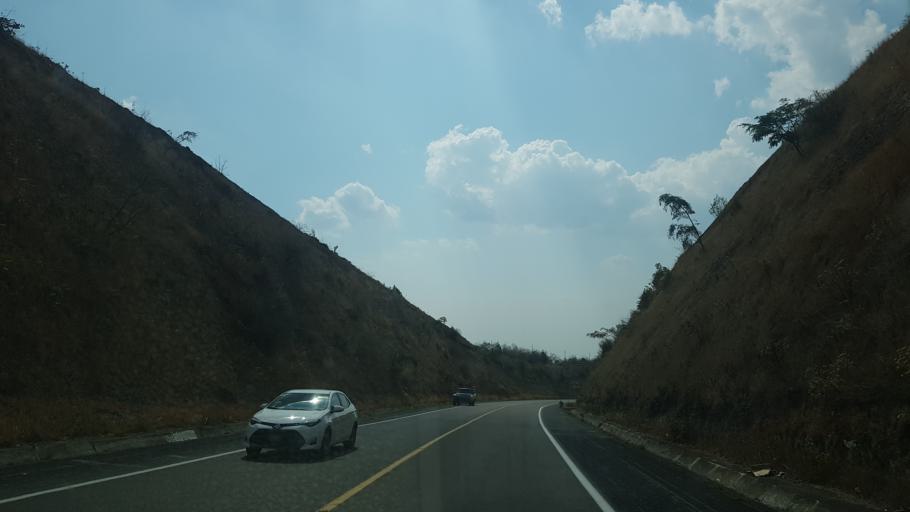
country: MX
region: Puebla
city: San Juan Amecac
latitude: 18.8155
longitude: -98.6739
